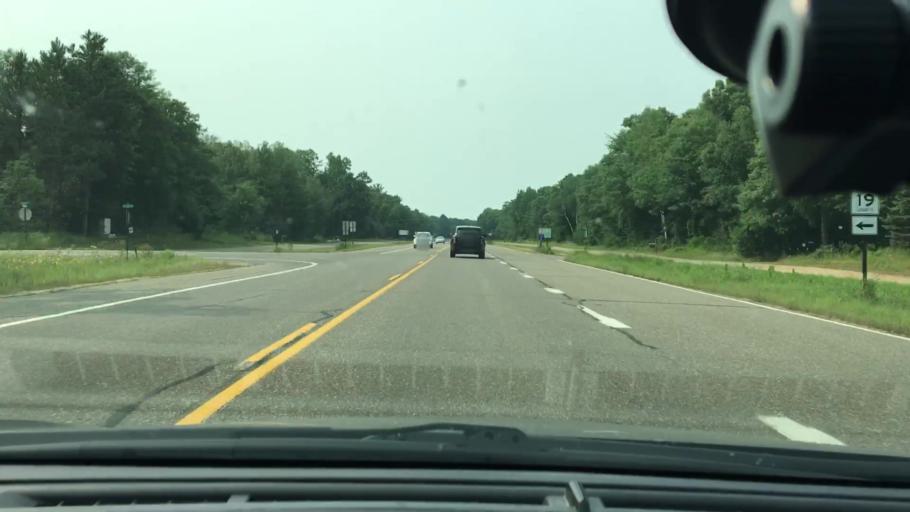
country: US
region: Minnesota
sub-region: Crow Wing County
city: Breezy Point
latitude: 46.5007
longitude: -94.1431
